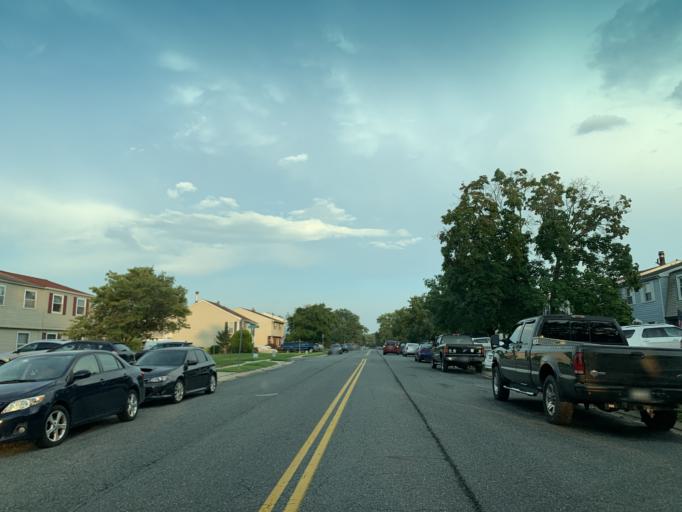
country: US
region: Maryland
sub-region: Harford County
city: Joppatowne
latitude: 39.4085
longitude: -76.3609
